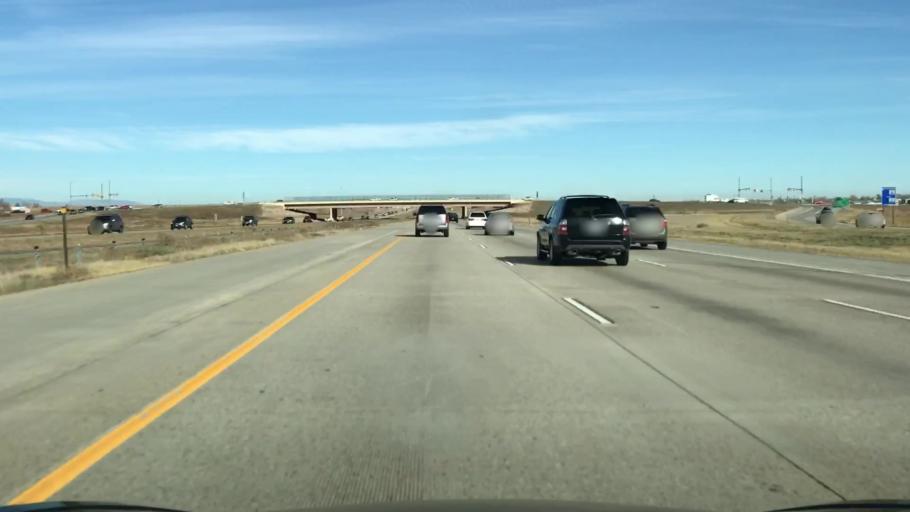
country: US
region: Colorado
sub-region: Weld County
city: Dacono
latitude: 40.0842
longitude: -104.9803
